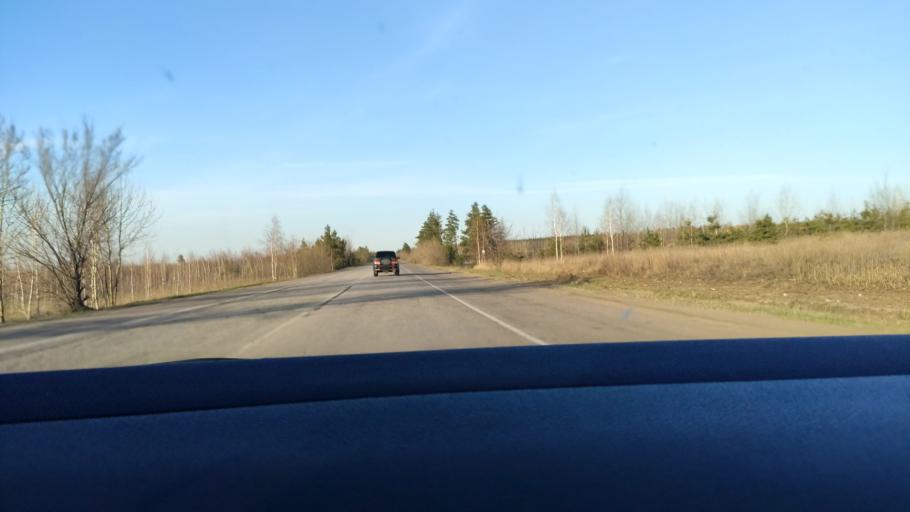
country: RU
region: Voronezj
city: Kolodeznyy
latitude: 51.3577
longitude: 39.1795
